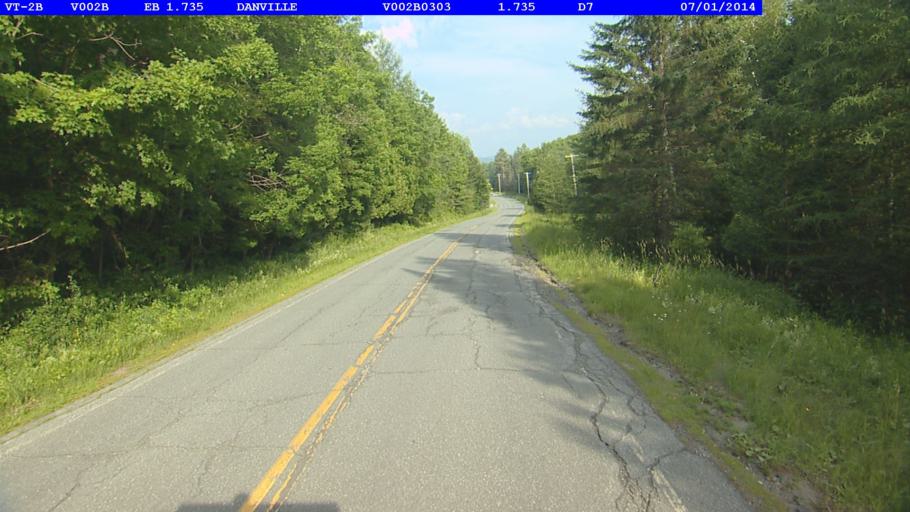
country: US
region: Vermont
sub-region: Caledonia County
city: St Johnsbury
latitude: 44.4307
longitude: -72.0591
